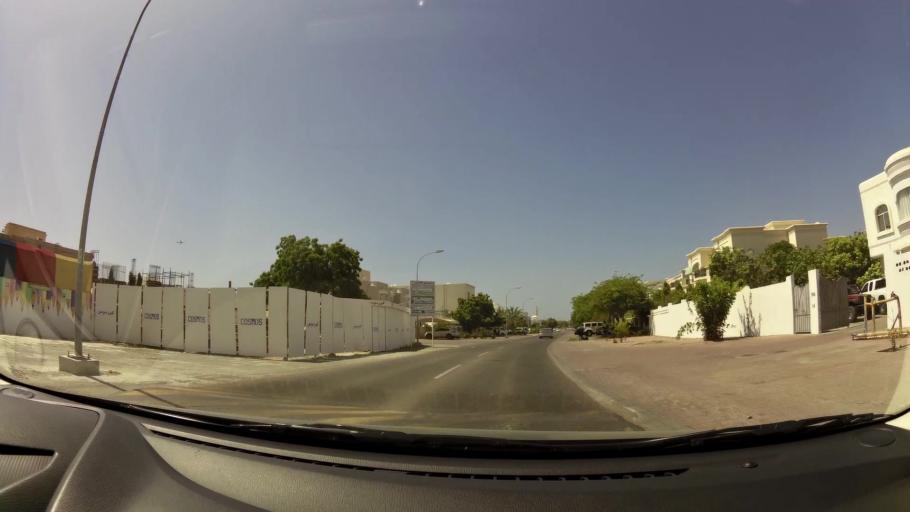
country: OM
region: Muhafazat Masqat
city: Bawshar
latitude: 23.5994
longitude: 58.3647
